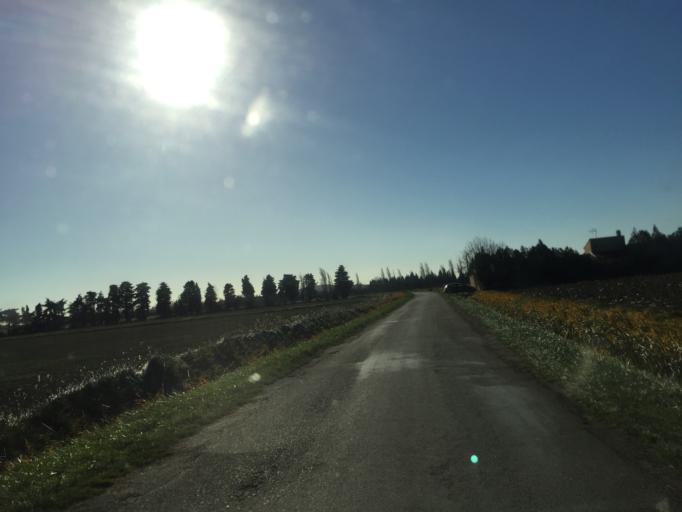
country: FR
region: Provence-Alpes-Cote d'Azur
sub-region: Departement du Vaucluse
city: Bedarrides
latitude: 44.0639
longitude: 4.9077
